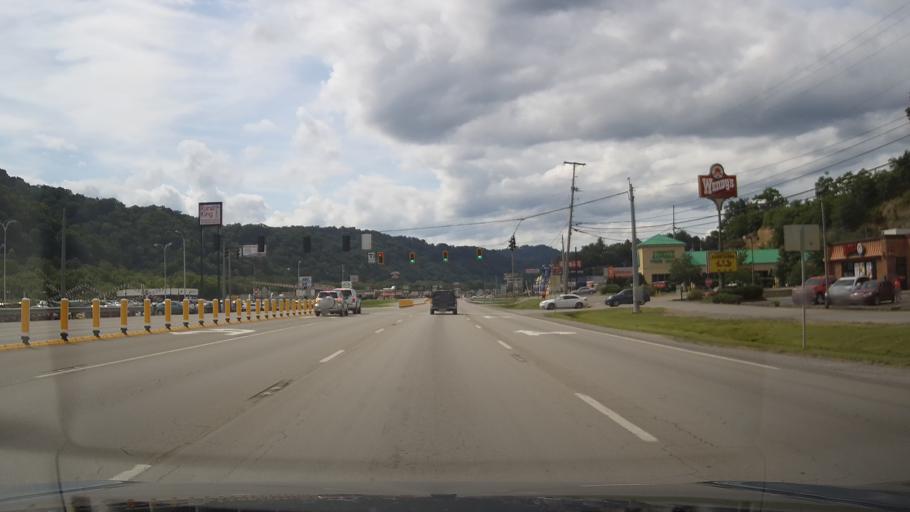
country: US
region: Kentucky
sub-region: Pike County
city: Coal Run Village
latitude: 37.5199
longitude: -82.5672
